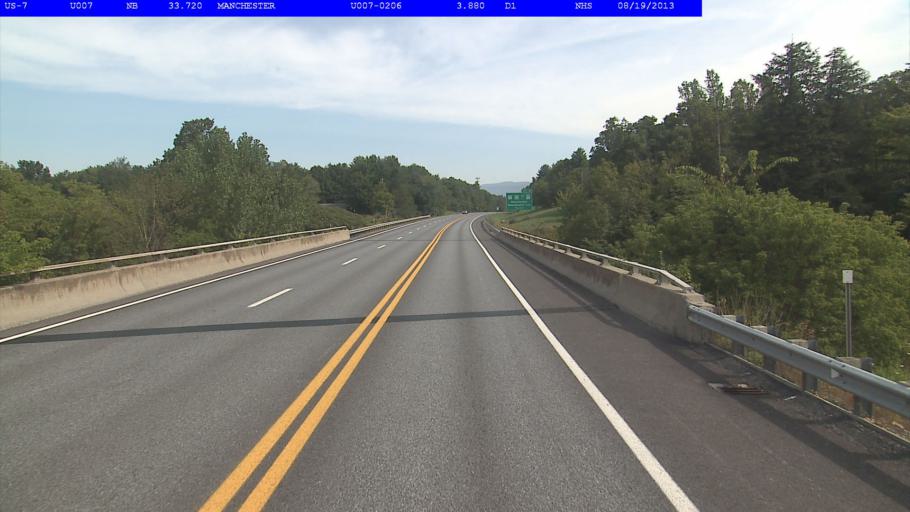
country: US
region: Vermont
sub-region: Bennington County
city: Manchester Center
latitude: 43.1648
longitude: -73.0403
